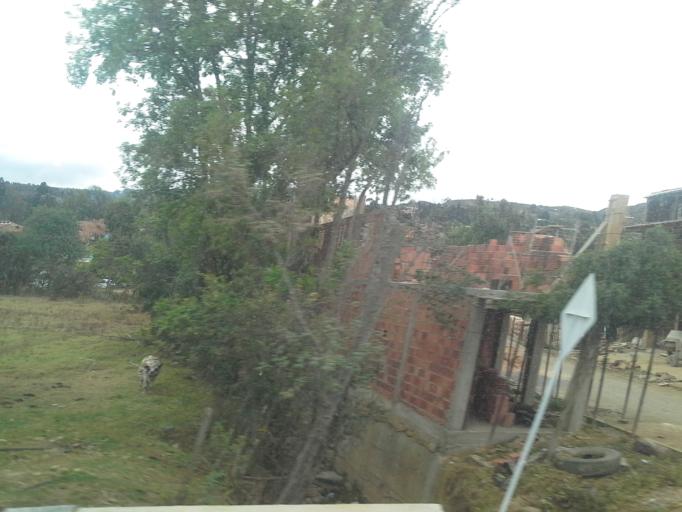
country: CO
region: Boyaca
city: Raquira
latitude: 5.5392
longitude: -73.6346
